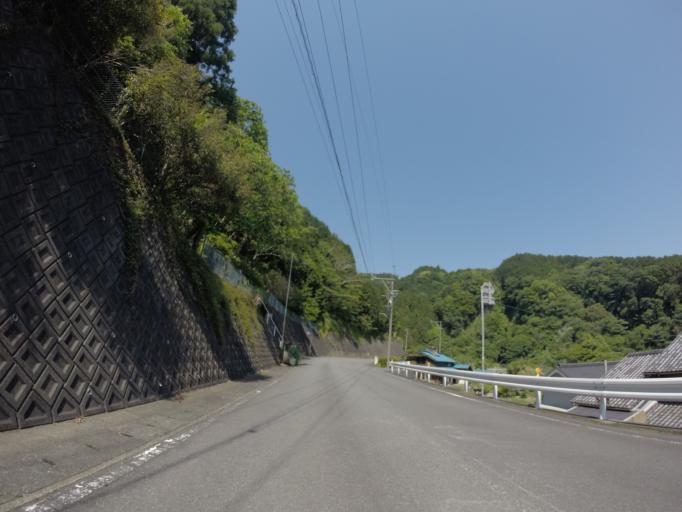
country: JP
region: Shizuoka
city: Fujinomiya
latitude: 35.1536
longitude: 138.5630
